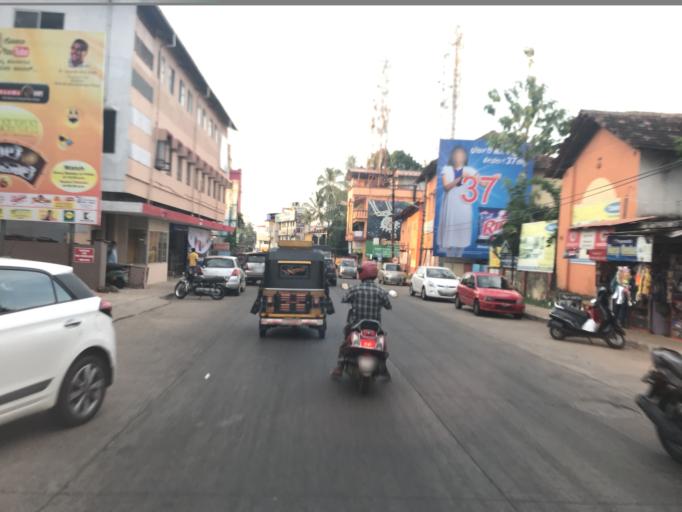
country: IN
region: Karnataka
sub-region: Dakshina Kannada
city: Mangalore
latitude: 12.8710
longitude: 74.8351
